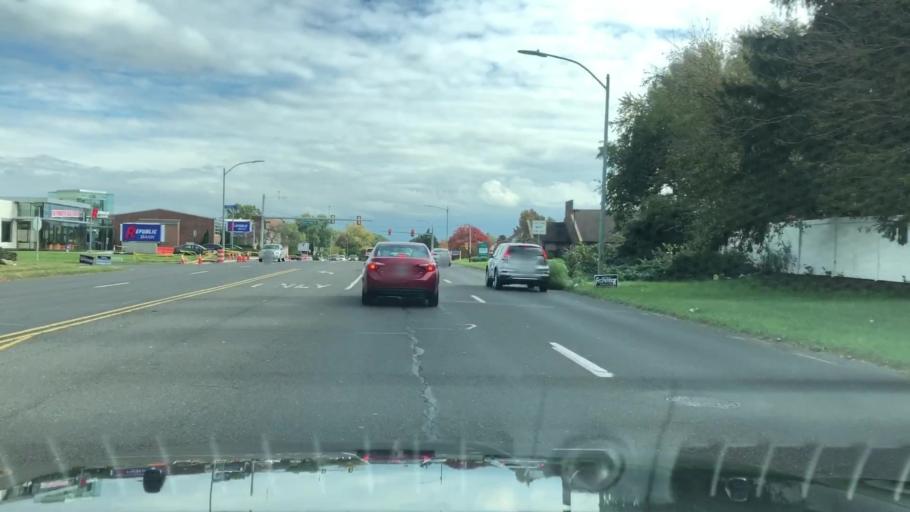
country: US
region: Pennsylvania
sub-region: Bucks County
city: Fairless Hills
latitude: 40.1675
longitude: -74.8470
